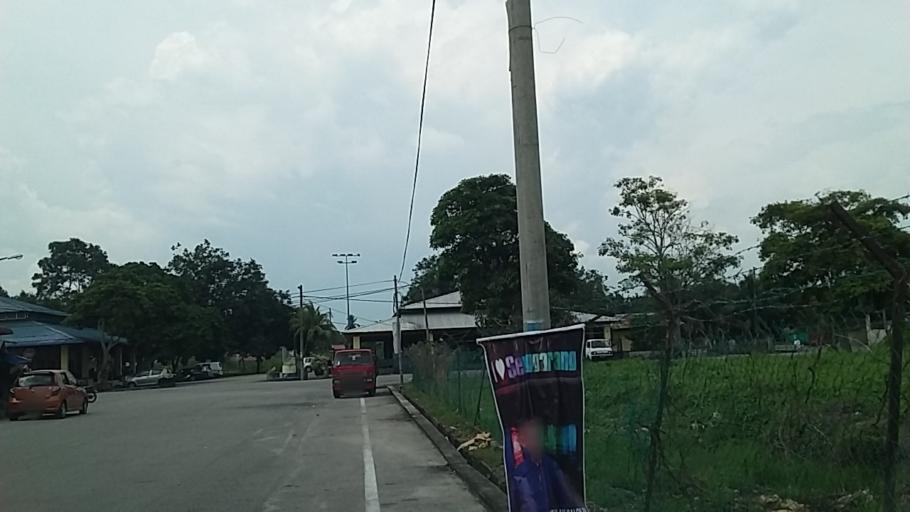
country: MY
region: Johor
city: Parit Raja
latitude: 1.7476
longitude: 103.0516
